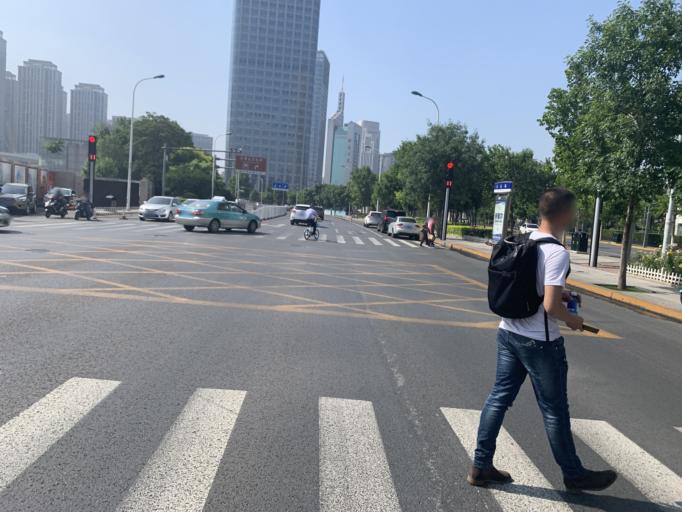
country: CN
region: Tianjin Shi
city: Quanyechang
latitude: 39.1287
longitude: 117.1901
